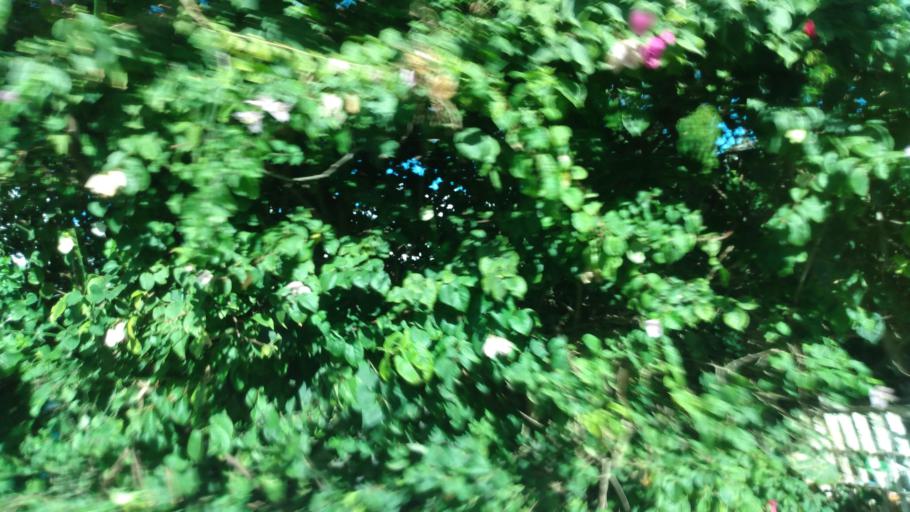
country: ET
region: Oromiya
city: Gore
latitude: 8.1992
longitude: 35.5673
